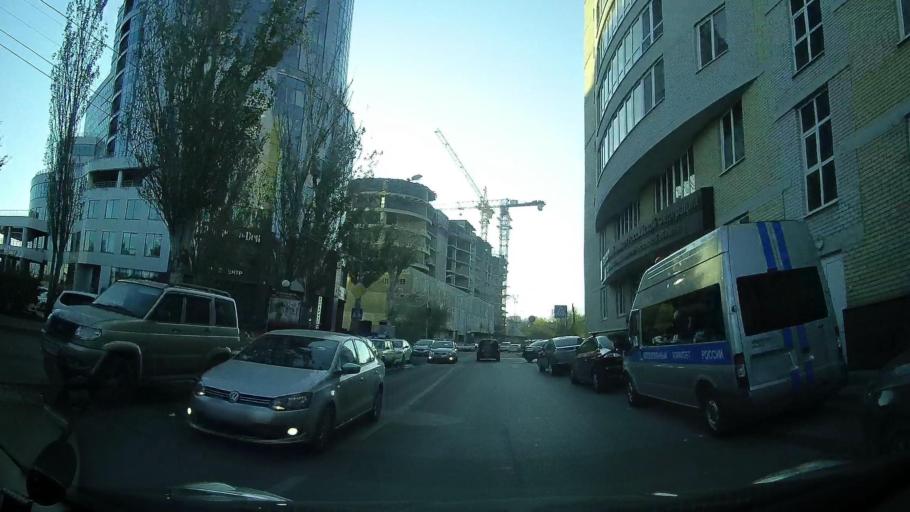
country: RU
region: Rostov
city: Rostov-na-Donu
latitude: 47.2129
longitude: 39.7057
